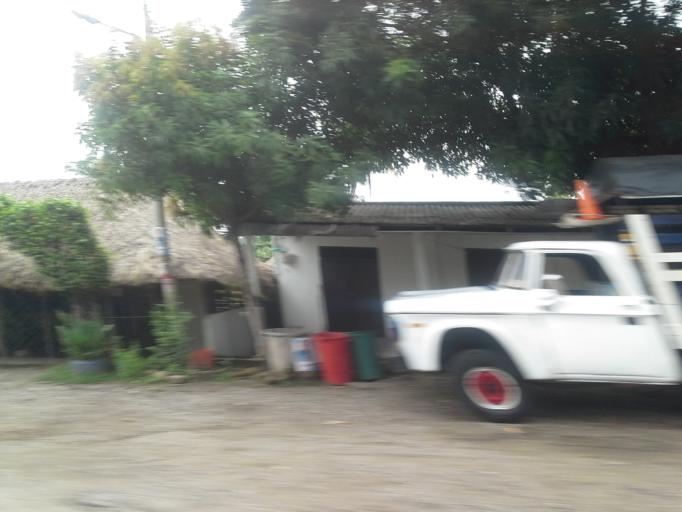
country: CO
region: Sucre
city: Ovejas
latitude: 9.5311
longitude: -75.2235
